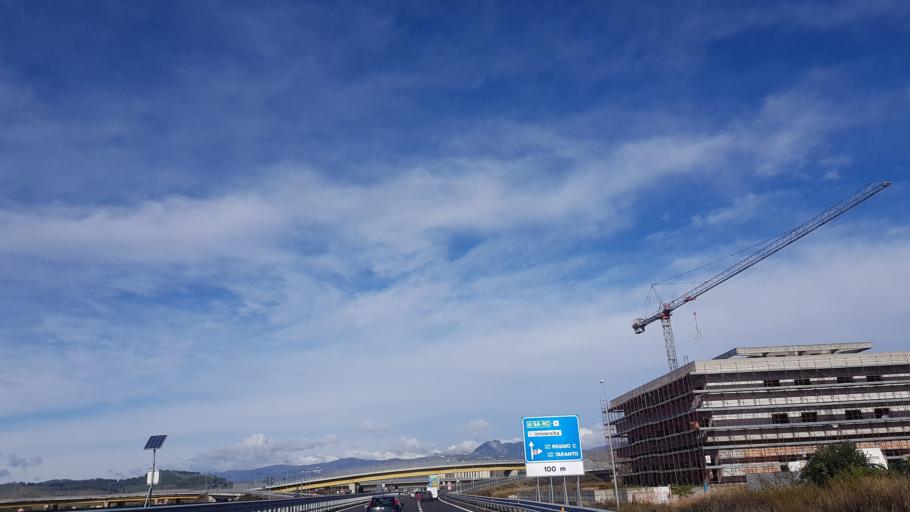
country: IT
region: Calabria
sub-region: Provincia di Catanzaro
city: Catanzaro
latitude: 38.8476
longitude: 16.5810
